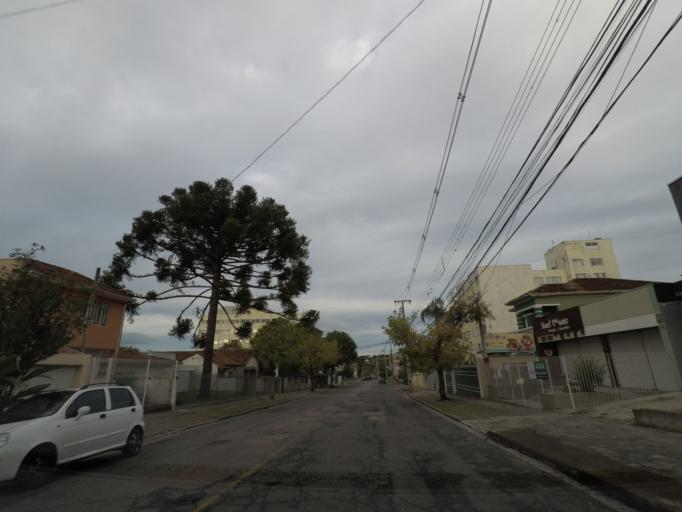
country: BR
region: Parana
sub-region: Curitiba
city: Curitiba
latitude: -25.4255
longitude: -49.2548
